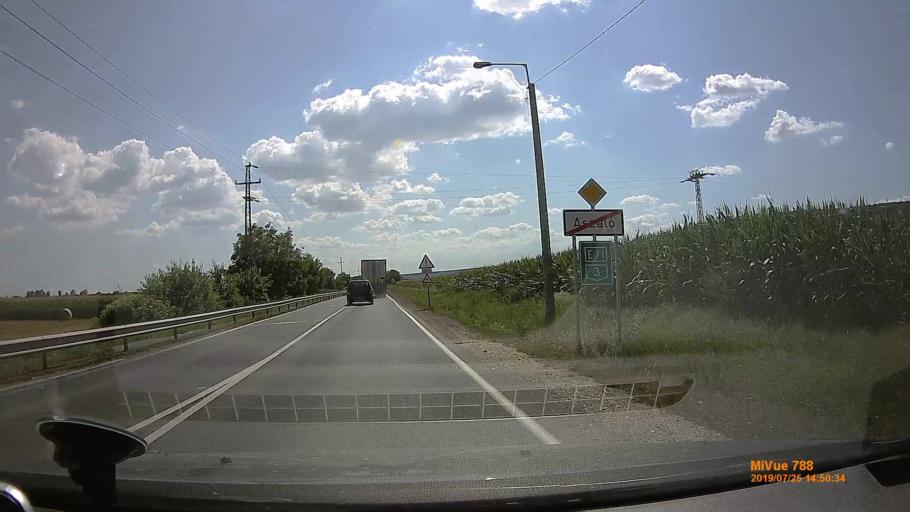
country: HU
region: Borsod-Abauj-Zemplen
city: Aszalo
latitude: 48.2220
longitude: 20.9512
